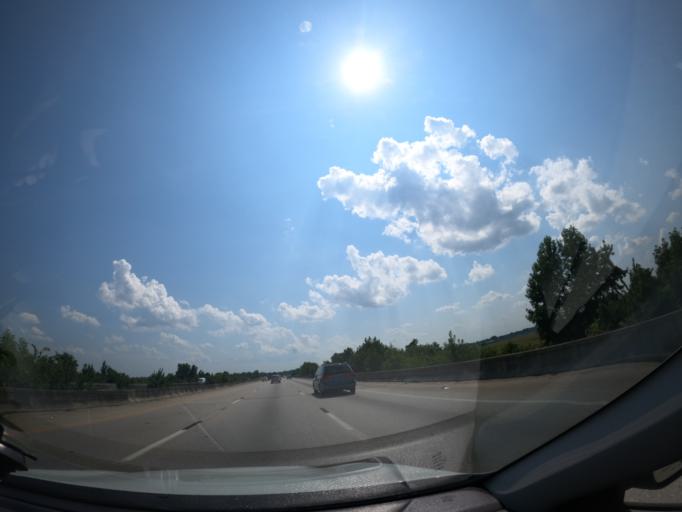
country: US
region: South Carolina
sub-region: Richland County
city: Columbia
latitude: 33.9411
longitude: -81.0044
